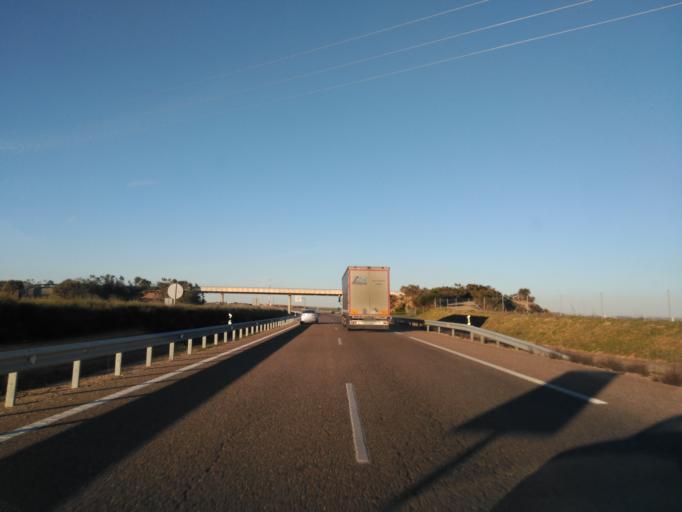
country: ES
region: Castille and Leon
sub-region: Provincia de Valladolid
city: Alaejos
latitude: 41.2954
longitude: -5.2337
